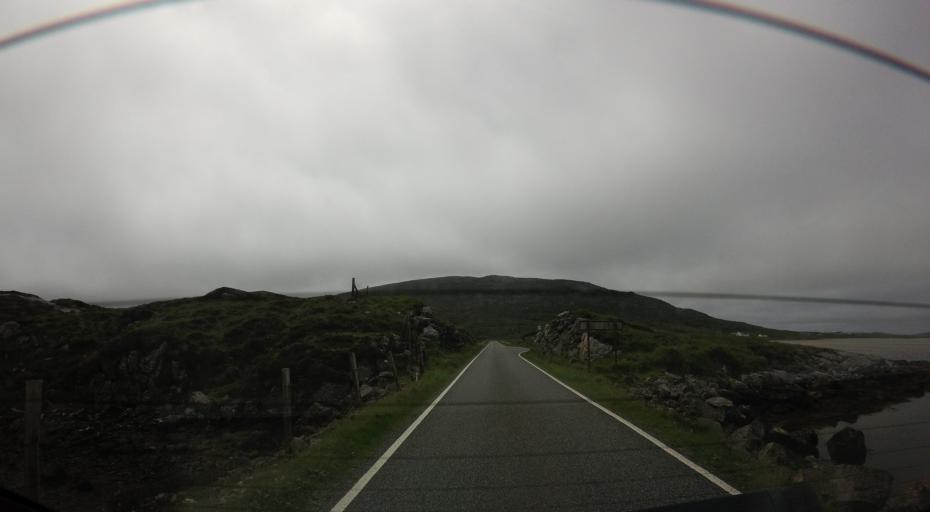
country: GB
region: Scotland
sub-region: Eilean Siar
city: Harris
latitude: 57.8666
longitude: -6.9156
